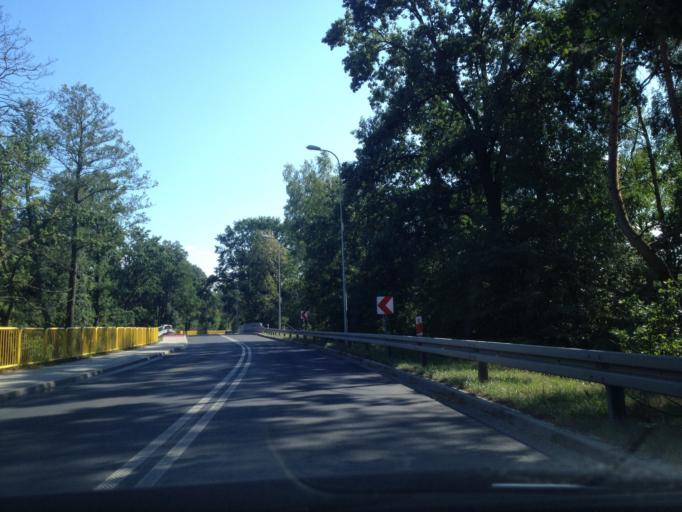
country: PL
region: Lubusz
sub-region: Powiat zaganski
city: Ilowa
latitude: 51.5189
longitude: 15.2137
